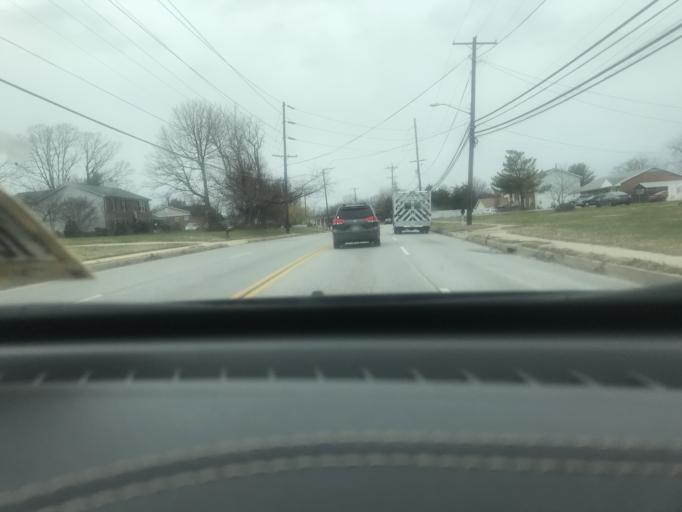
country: US
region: Maryland
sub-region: Prince George's County
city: Temple Hills
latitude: 38.7907
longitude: -76.9342
